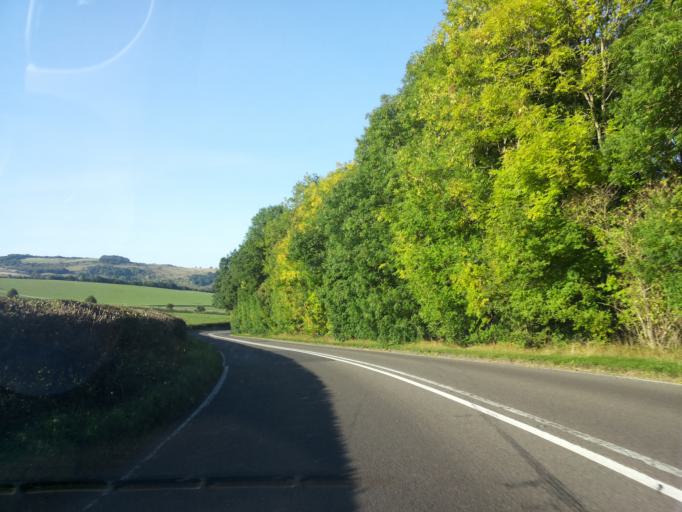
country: GB
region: England
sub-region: Derbyshire
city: Bakewell
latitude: 53.2322
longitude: -1.6555
